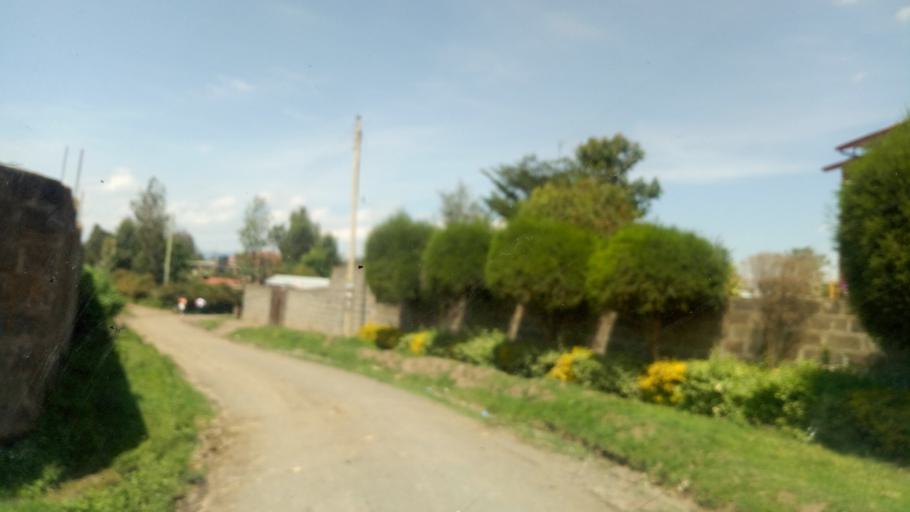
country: KE
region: Nakuru
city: Nakuru
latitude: -0.2759
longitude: 36.1121
